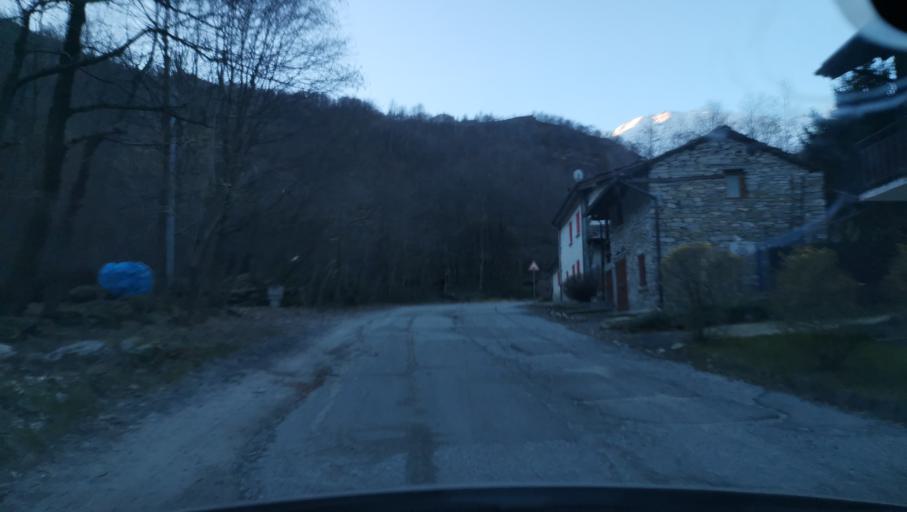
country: IT
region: Piedmont
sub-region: Provincia di Torino
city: Rora
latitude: 44.7701
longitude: 7.2049
